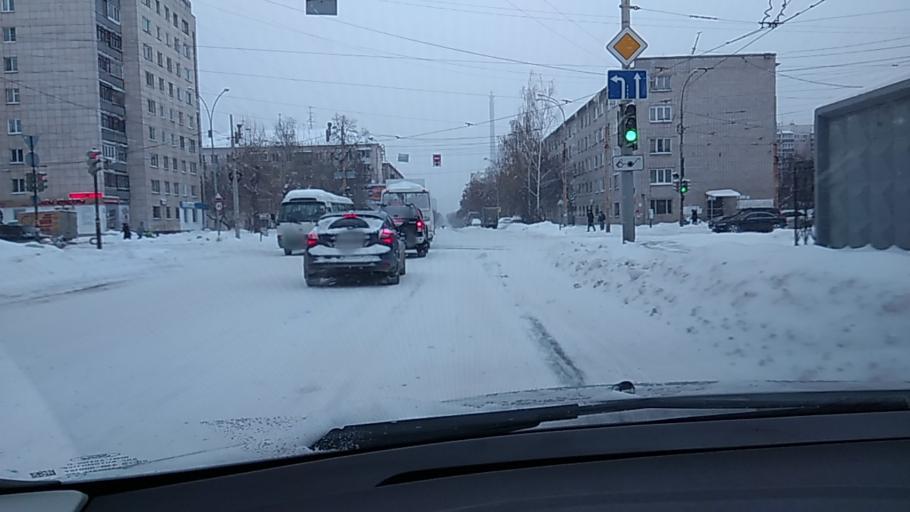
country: RU
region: Sverdlovsk
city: Yekaterinburg
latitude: 56.8131
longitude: 60.6115
